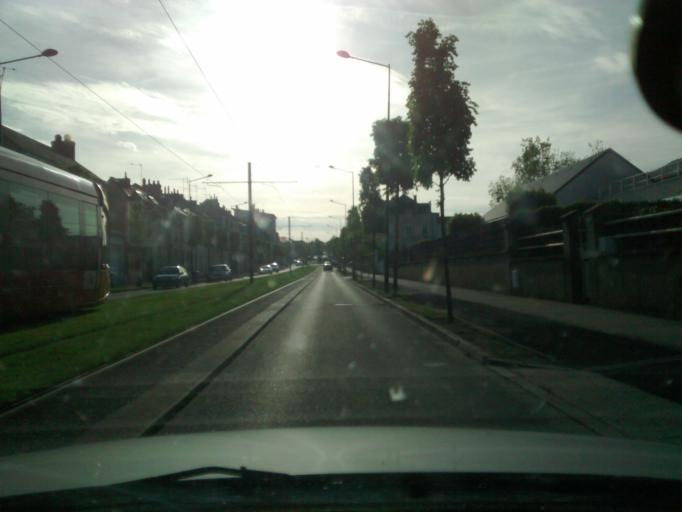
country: FR
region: Pays de la Loire
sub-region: Departement de la Sarthe
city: Le Mans
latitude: 48.0127
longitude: 0.1792
